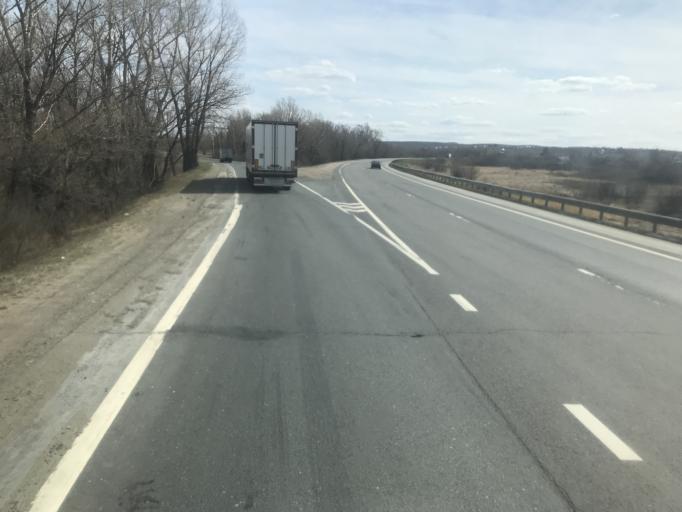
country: RU
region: Samara
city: Novosemeykino
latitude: 53.4177
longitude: 50.3332
